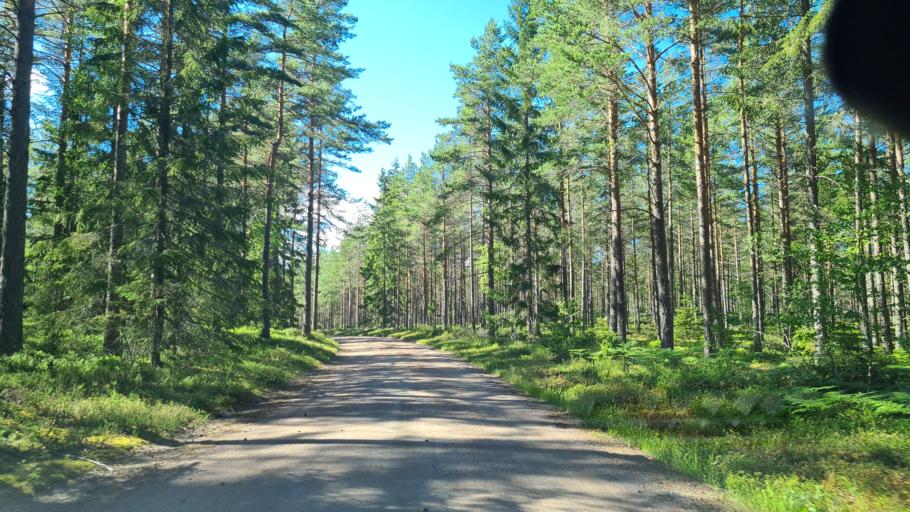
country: SE
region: OEstergoetland
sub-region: Norrkopings Kommun
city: Krokek
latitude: 58.6922
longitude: 16.4323
